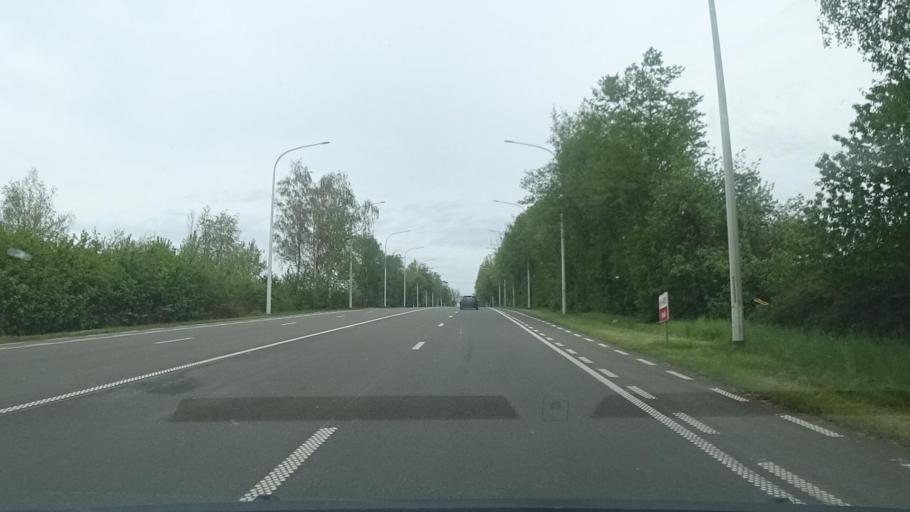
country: BE
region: Wallonia
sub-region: Province de Namur
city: Floreffe
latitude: 50.5035
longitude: 4.7805
